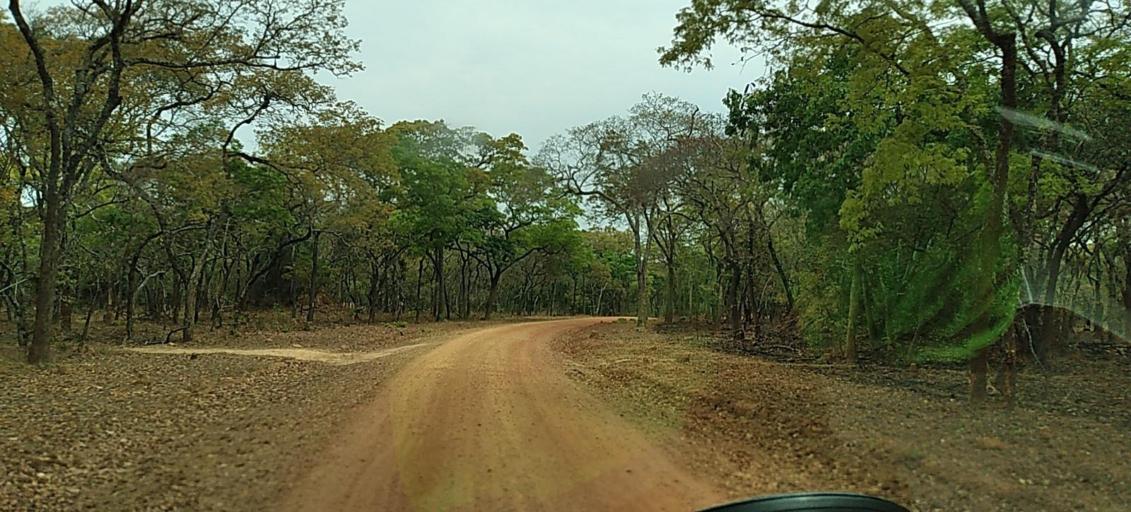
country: ZM
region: North-Western
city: Solwezi
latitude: -12.9231
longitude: 26.5613
